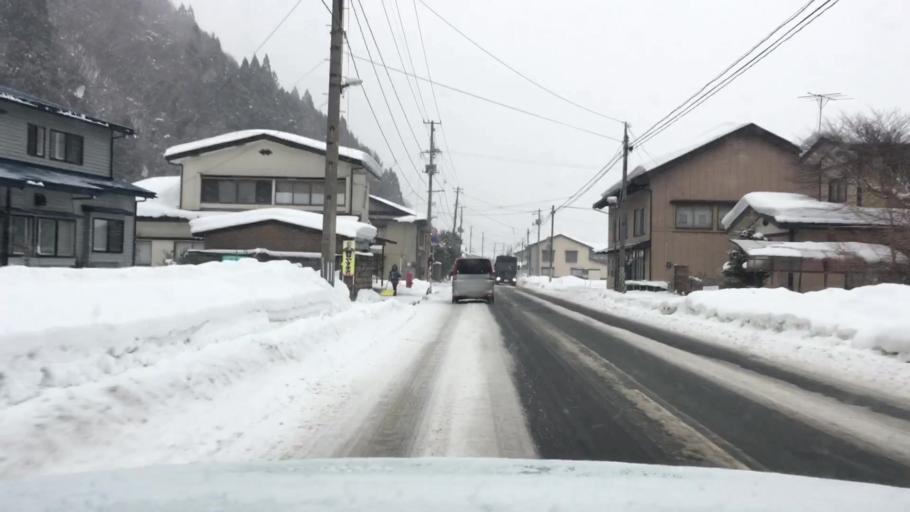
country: JP
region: Iwate
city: Ichinohe
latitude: 40.0934
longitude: 141.0470
